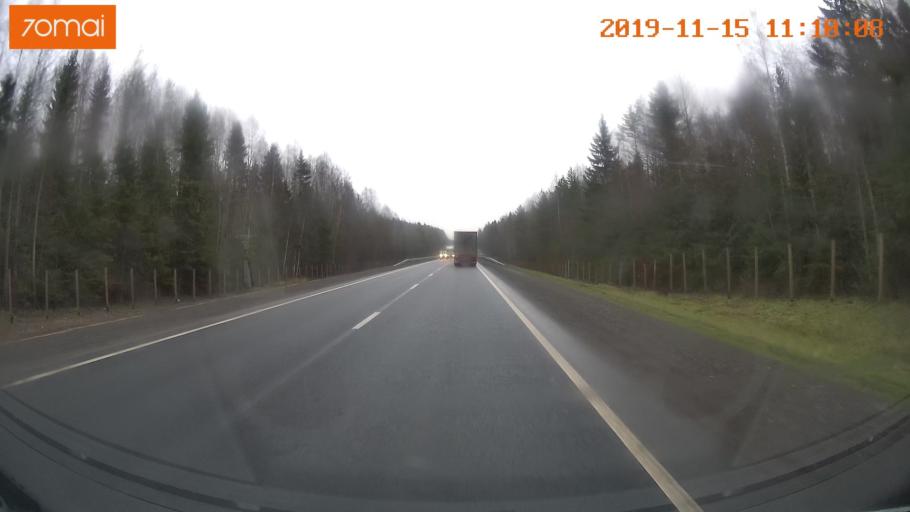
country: RU
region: Vologda
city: Chebsara
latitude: 59.1209
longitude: 39.1156
